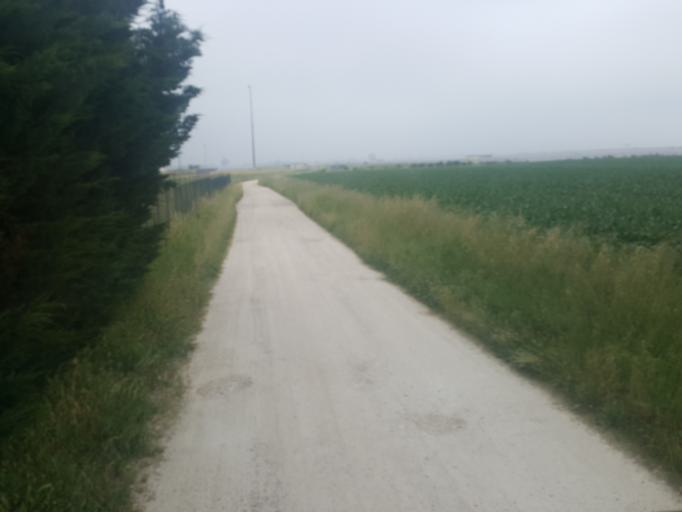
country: IT
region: Veneto
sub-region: Provincia di Rovigo
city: Canaro
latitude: 44.9390
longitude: 11.6491
